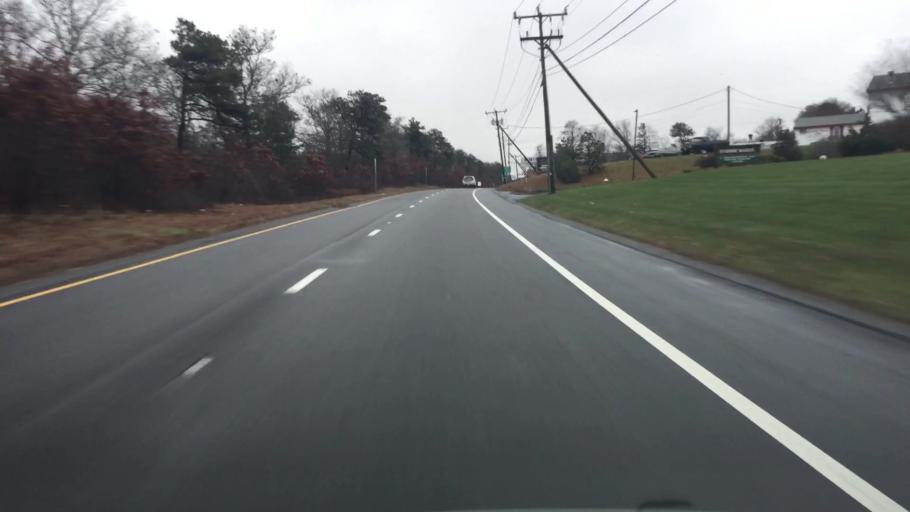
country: US
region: Massachusetts
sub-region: Barnstable County
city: Bourne
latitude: 41.7347
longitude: -70.5846
